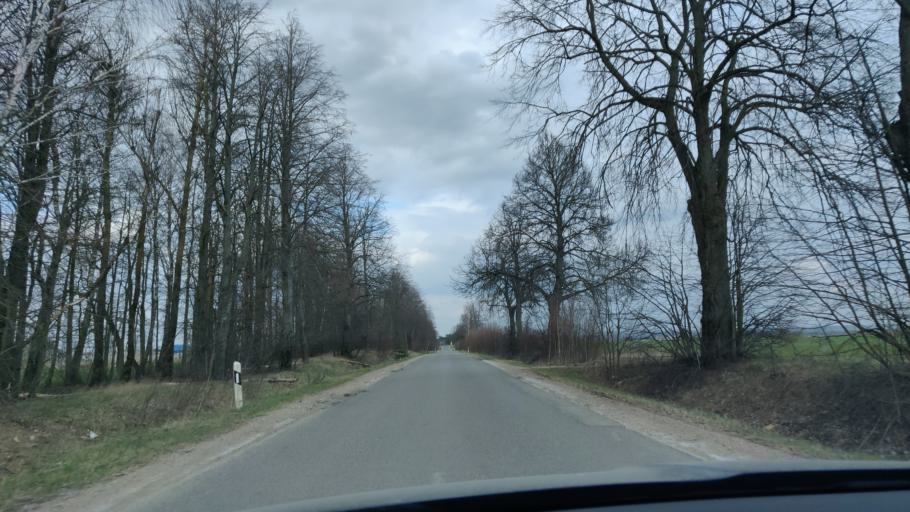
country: LT
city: Lentvaris
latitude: 54.6081
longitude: 25.1140
